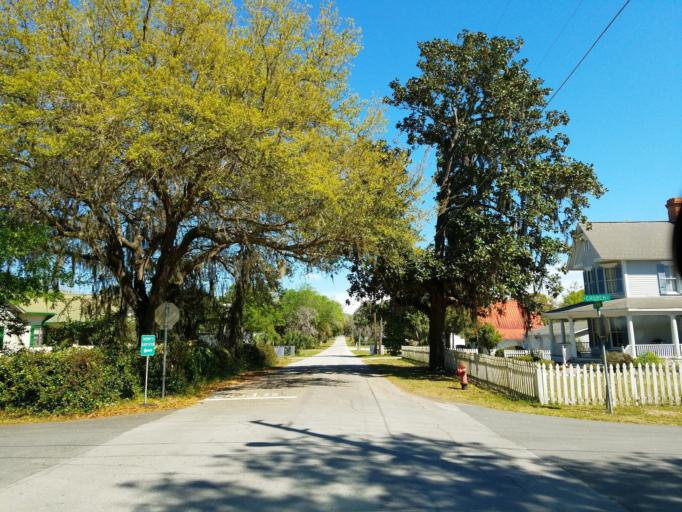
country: US
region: Florida
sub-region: Sumter County
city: Lake Panasoffkee
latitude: 28.8017
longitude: -82.0686
